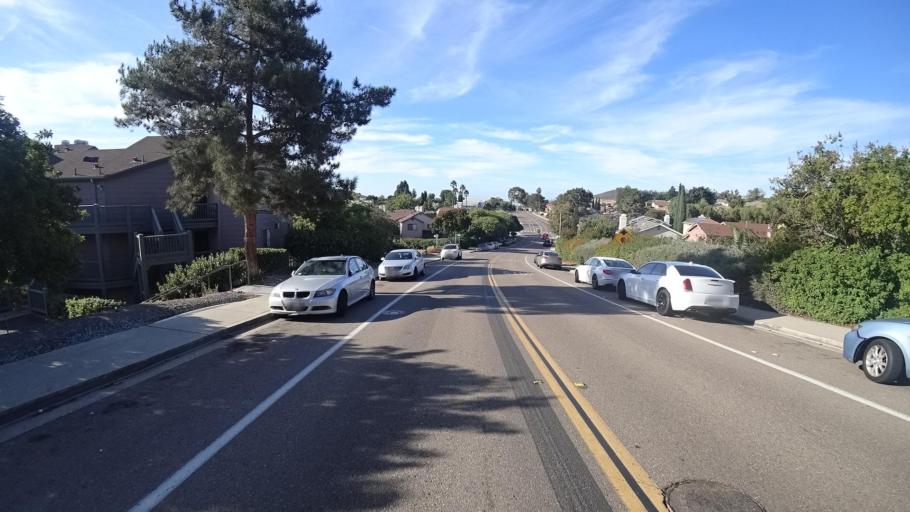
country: US
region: California
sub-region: San Diego County
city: Rancho San Diego
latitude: 32.7345
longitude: -116.9618
